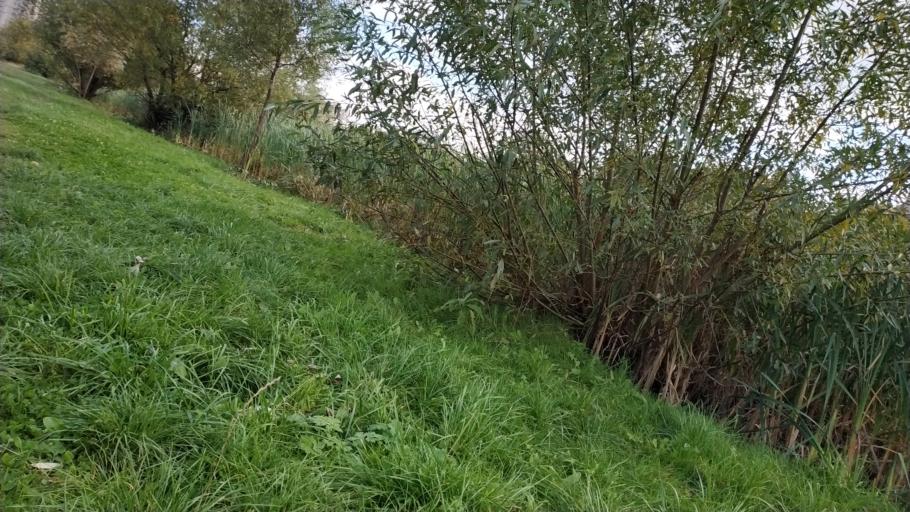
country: RU
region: Moscow
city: Metrogorodok
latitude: 55.7948
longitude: 37.7633
